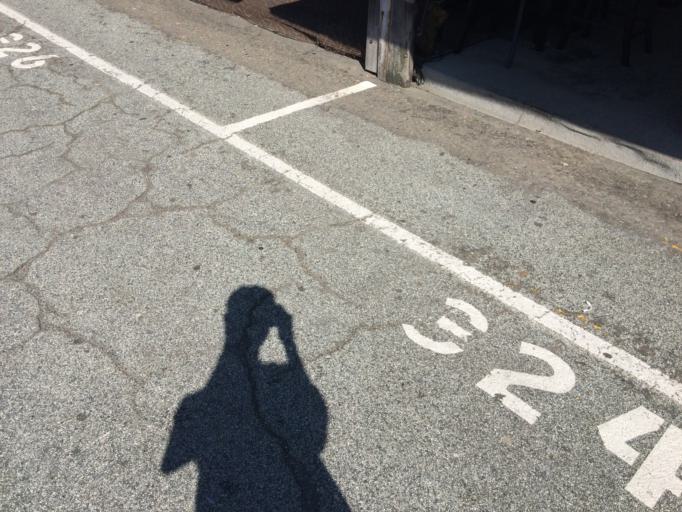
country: US
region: California
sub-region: Santa Clara County
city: San Jose
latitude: 37.3685
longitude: -121.8766
